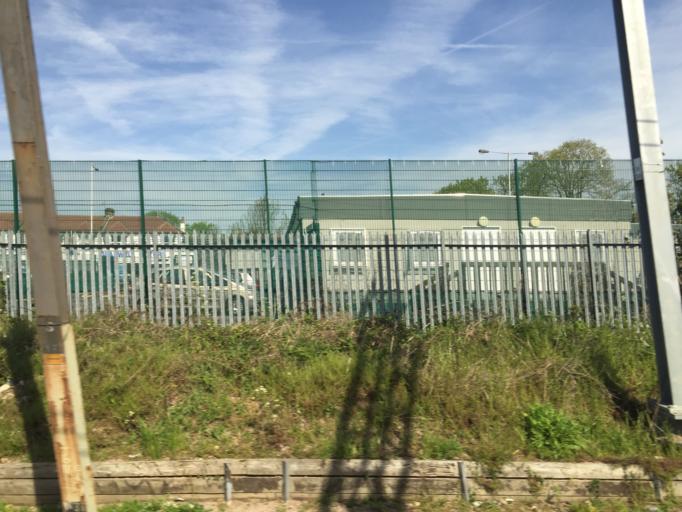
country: GB
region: England
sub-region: Greater London
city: Becontree
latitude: 51.5644
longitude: 0.1023
